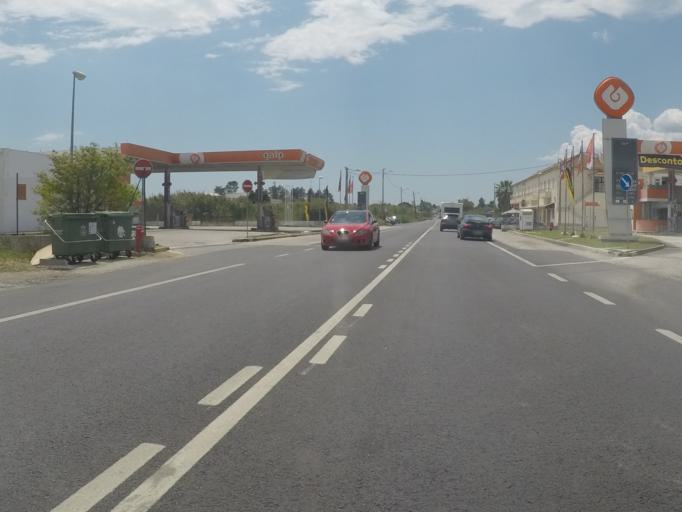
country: PT
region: Setubal
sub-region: Setubal
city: Setubal
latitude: 38.5501
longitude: -8.8111
